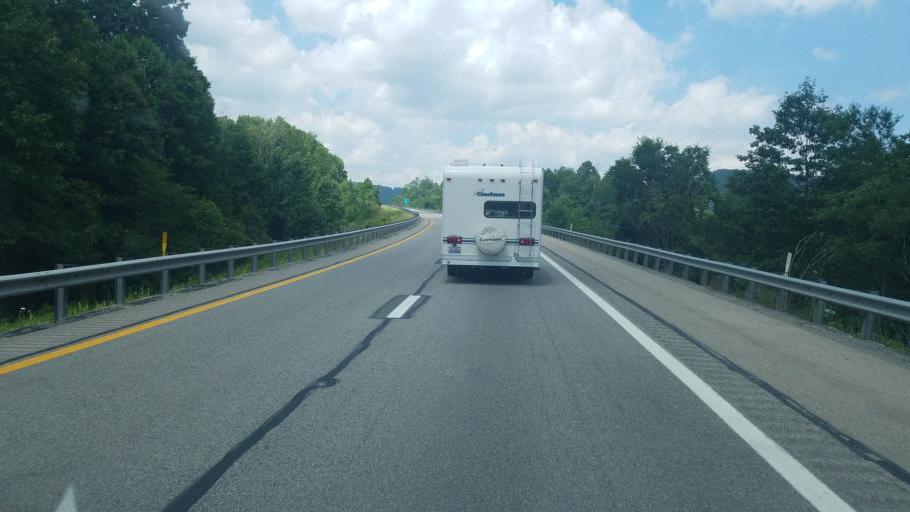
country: US
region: West Virginia
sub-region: Raleigh County
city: Bradley
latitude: 37.9031
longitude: -81.2657
